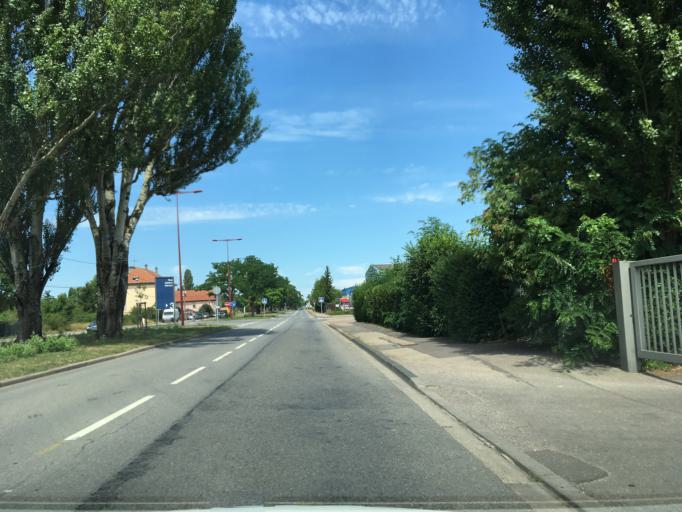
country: FR
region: Lorraine
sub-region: Departement de la Moselle
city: Metz
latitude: 49.1392
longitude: 6.1727
